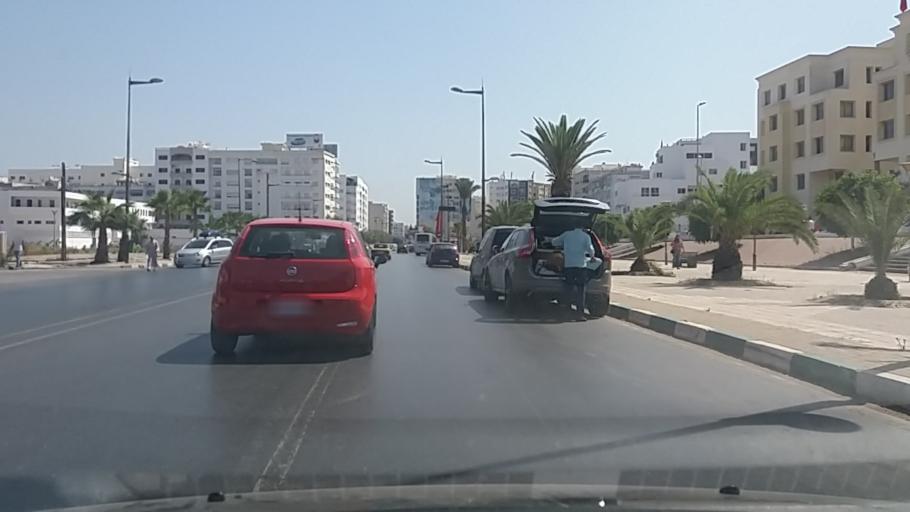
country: MA
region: Gharb-Chrarda-Beni Hssen
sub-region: Kenitra Province
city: Kenitra
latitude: 34.2546
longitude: -6.5985
